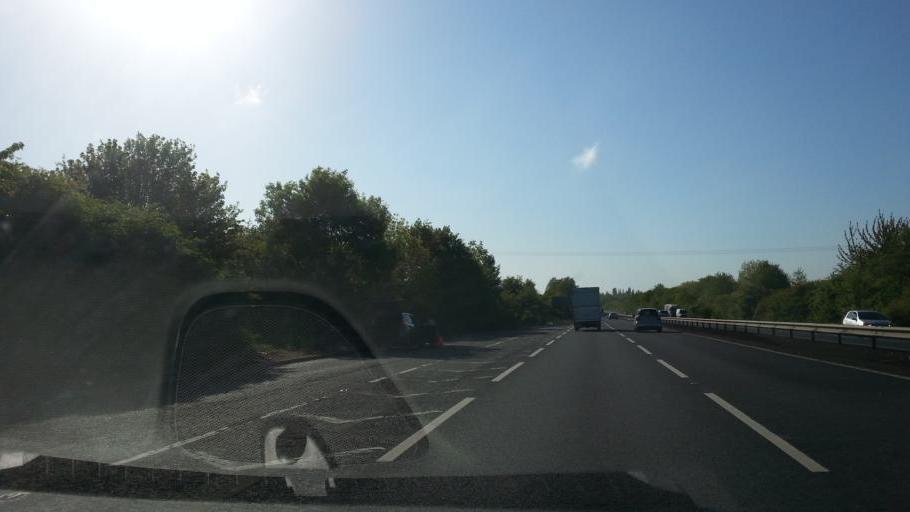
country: GB
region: England
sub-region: Peterborough
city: Castor
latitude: 52.5772
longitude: -0.3379
